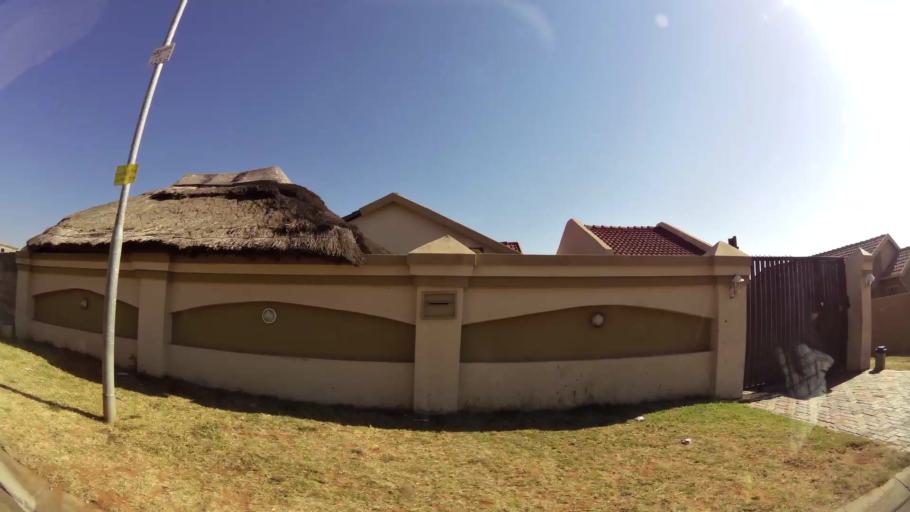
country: ZA
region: Gauteng
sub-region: Ekurhuleni Metropolitan Municipality
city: Tembisa
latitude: -26.0392
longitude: 28.2027
